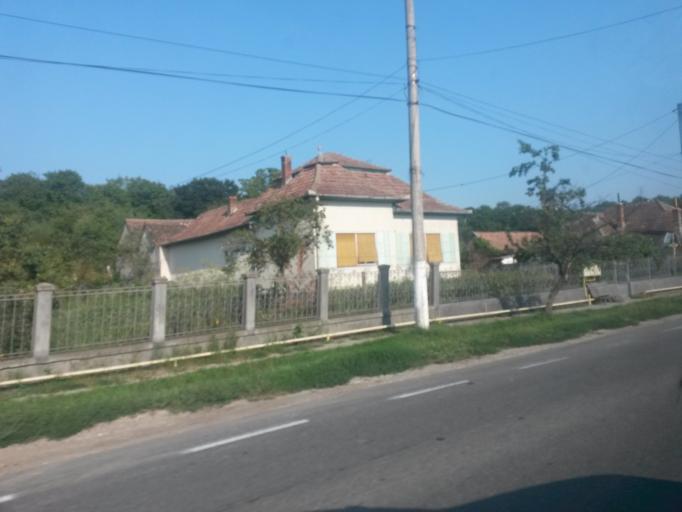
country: RO
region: Alba
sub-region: Comuna Unirea
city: Unirea
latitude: 46.4095
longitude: 23.8093
